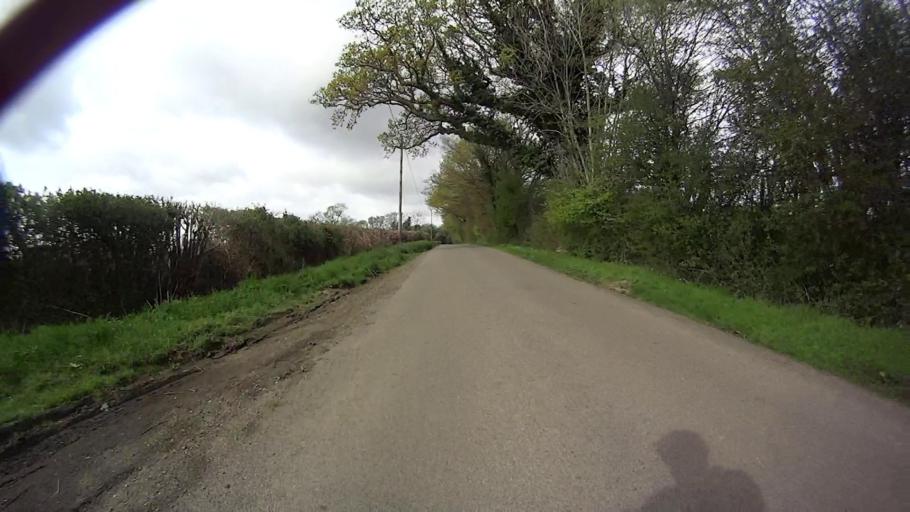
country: GB
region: England
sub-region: West Sussex
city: Bewbush
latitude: 51.1295
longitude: -0.2508
